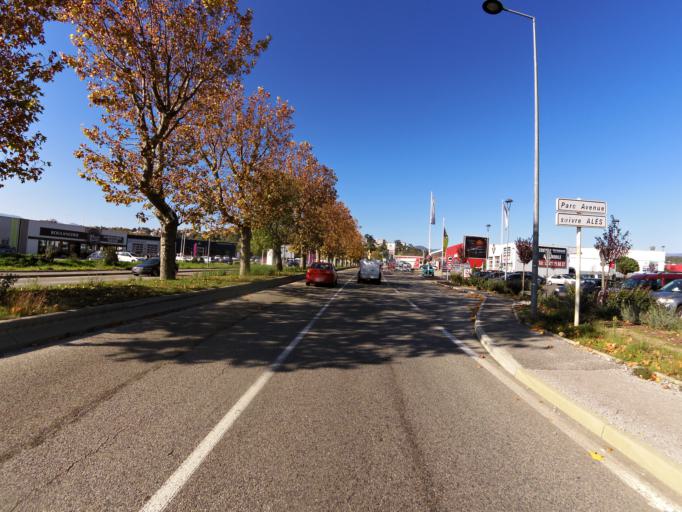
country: FR
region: Rhone-Alpes
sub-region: Departement de l'Ardeche
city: Aubenas
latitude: 44.6132
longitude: 4.4076
